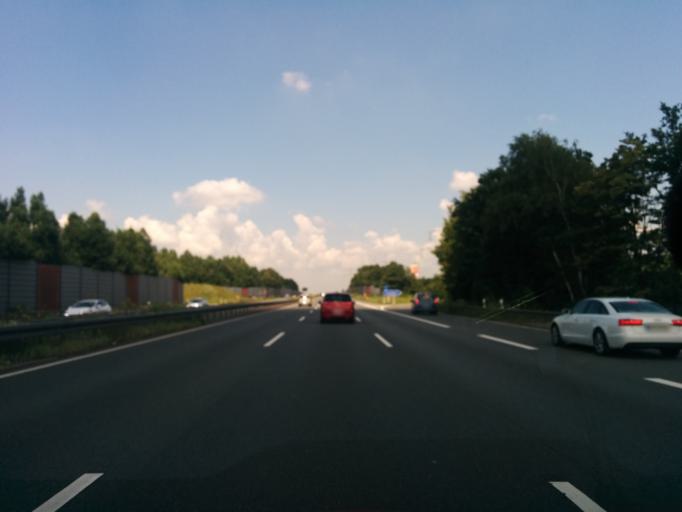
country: DE
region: Lower Saxony
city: Rosdorf
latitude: 51.5217
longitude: 9.8789
